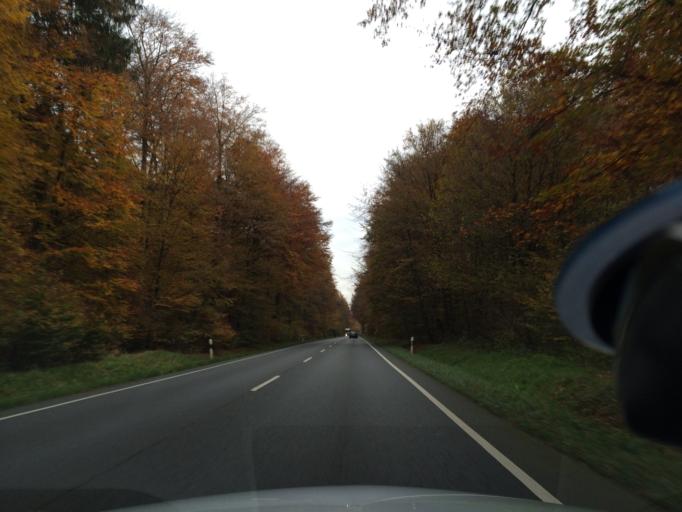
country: DE
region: Hesse
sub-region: Regierungsbezirk Darmstadt
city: Dietzenbach
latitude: 50.0443
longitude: 8.7587
